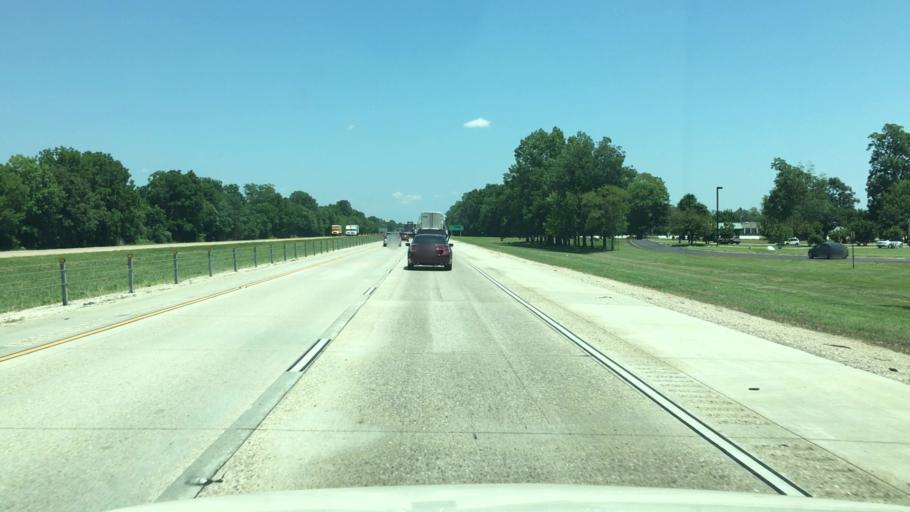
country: US
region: Arkansas
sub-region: Miller County
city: Texarkana
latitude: 33.5169
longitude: -93.9378
